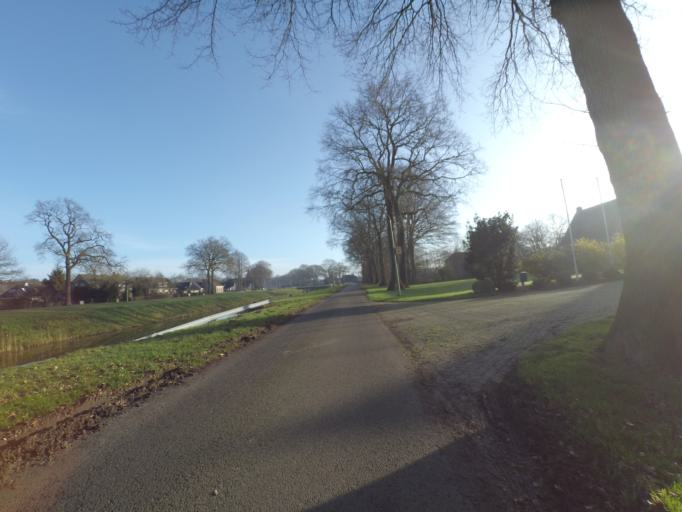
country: NL
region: Drenthe
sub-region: Gemeente Coevorden
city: Sleen
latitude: 52.8412
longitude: 6.7181
